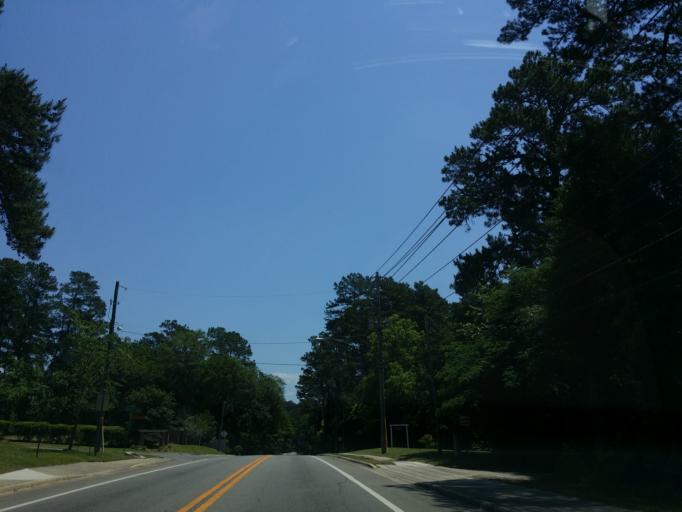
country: US
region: Florida
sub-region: Leon County
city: Tallahassee
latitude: 30.4738
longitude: -84.3277
